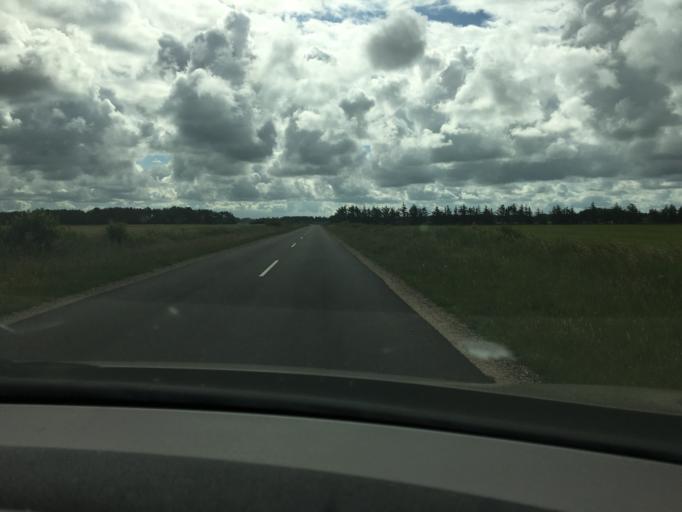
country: DK
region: Central Jutland
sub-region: Ringkobing-Skjern Kommune
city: Hvide Sande
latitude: 55.8306
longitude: 8.2190
